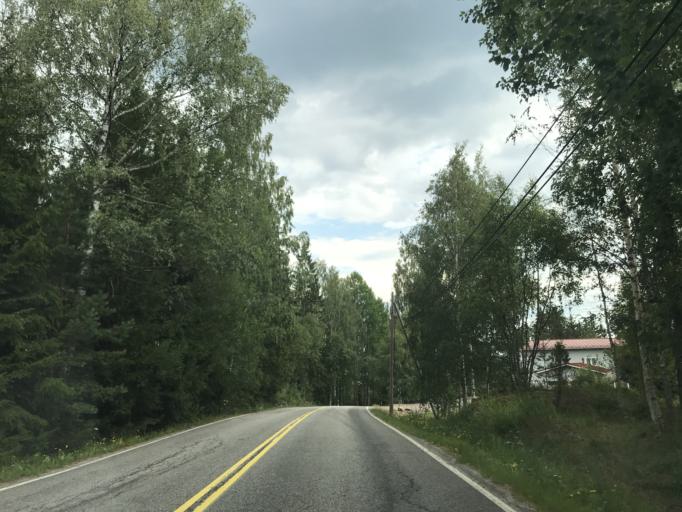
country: FI
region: Uusimaa
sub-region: Helsinki
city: Vihti
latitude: 60.3893
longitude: 24.3417
